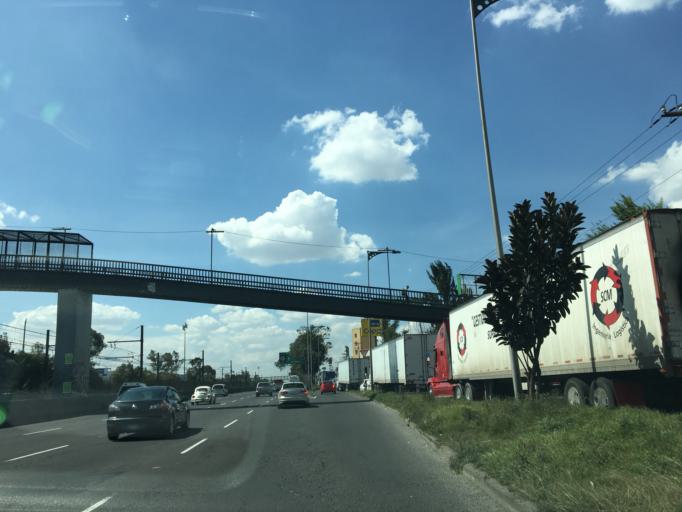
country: MX
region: Mexico City
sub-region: Iztacalco
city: Iztacalco
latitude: 19.3995
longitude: -99.0603
